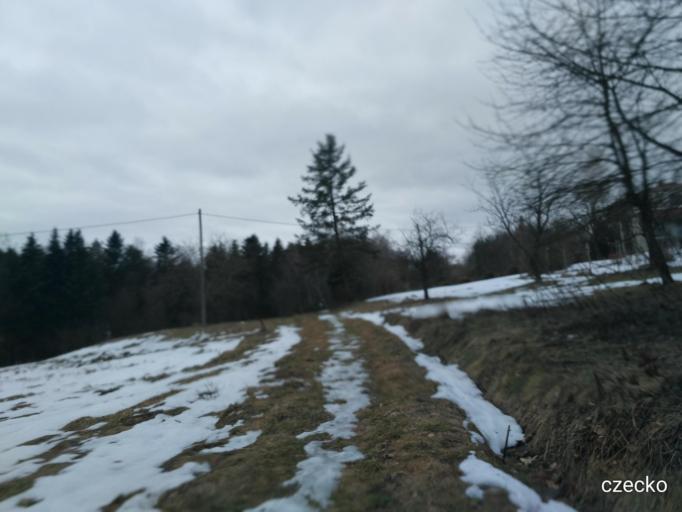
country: PL
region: Subcarpathian Voivodeship
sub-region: Powiat krosnienski
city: Korczyna
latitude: 49.7469
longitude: 21.8258
